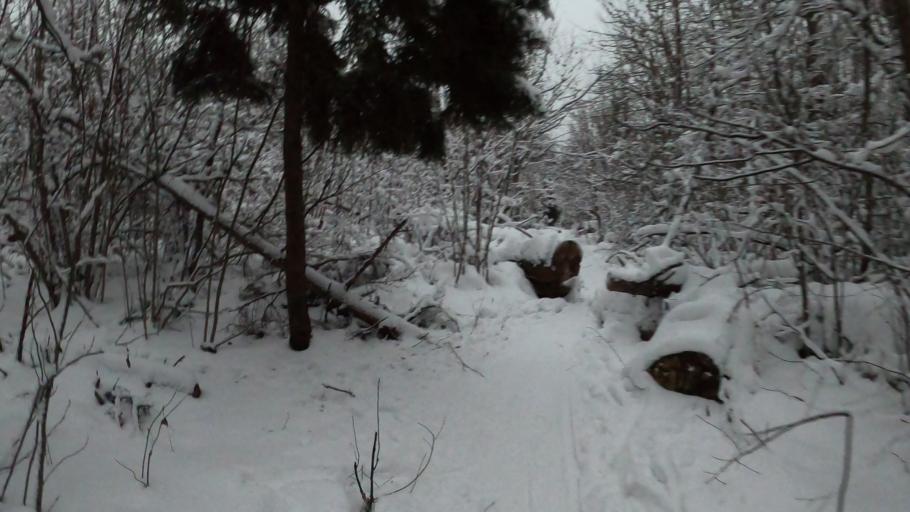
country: RU
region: Moskovskaya
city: Nakhabino
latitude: 55.8965
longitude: 37.2075
